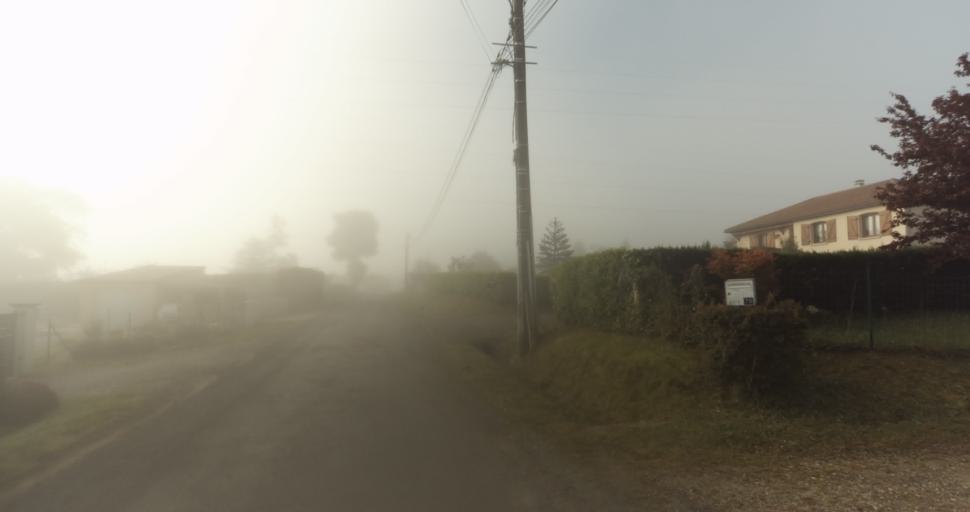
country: FR
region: Limousin
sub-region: Departement de la Haute-Vienne
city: Condat-sur-Vienne
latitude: 45.7841
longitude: 1.2755
